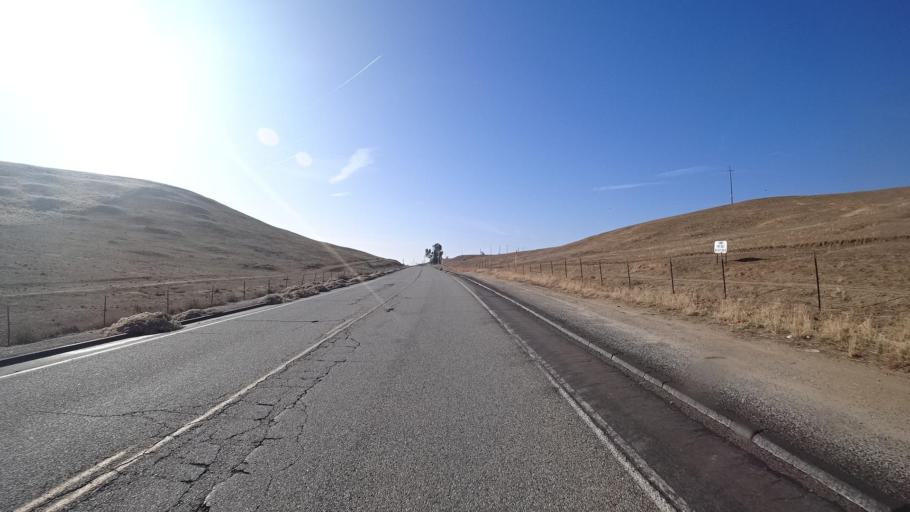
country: US
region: California
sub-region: Kern County
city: Oildale
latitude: 35.4985
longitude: -118.9950
